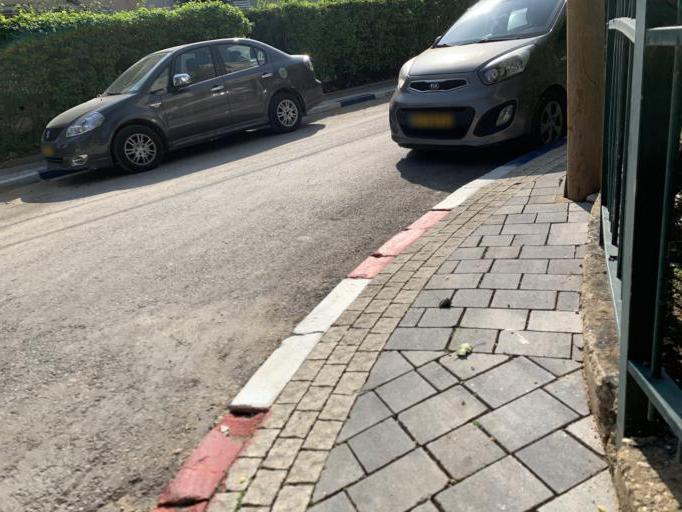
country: IL
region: Tel Aviv
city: Ramat Gan
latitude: 32.0936
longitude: 34.8164
